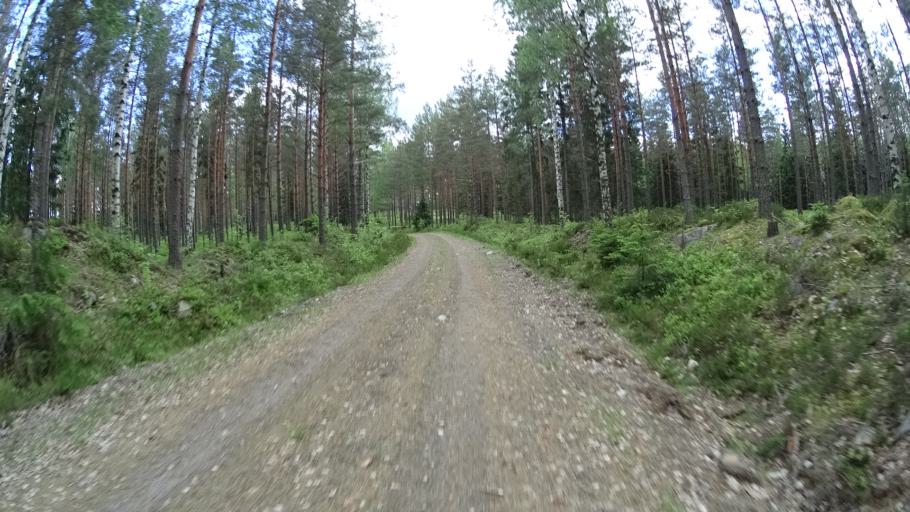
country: FI
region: Varsinais-Suomi
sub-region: Salo
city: Kisko
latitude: 60.1814
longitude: 23.5566
